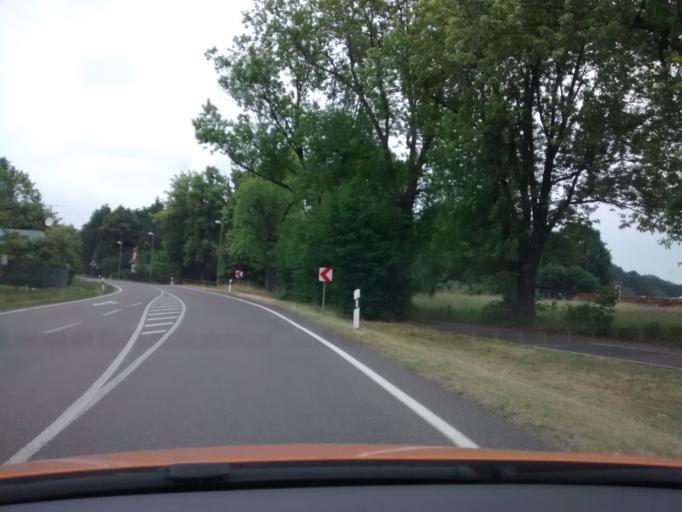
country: DE
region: Brandenburg
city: Wiesenburg
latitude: 52.0886
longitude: 12.4447
